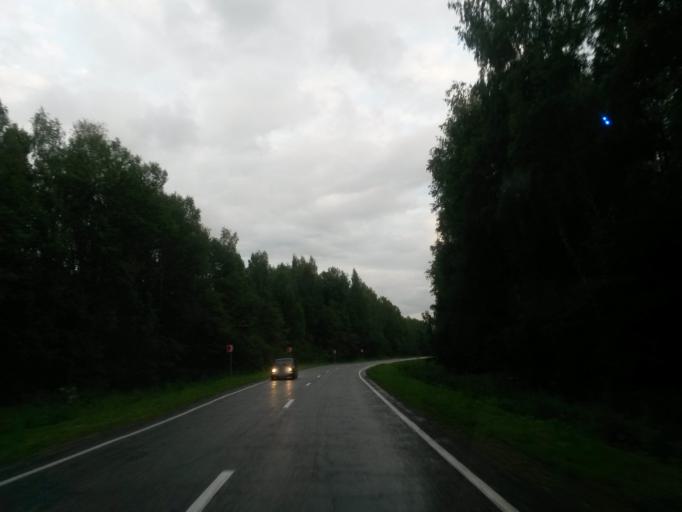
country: RU
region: Jaroslavl
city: Tutayev
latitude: 57.9180
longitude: 39.5150
